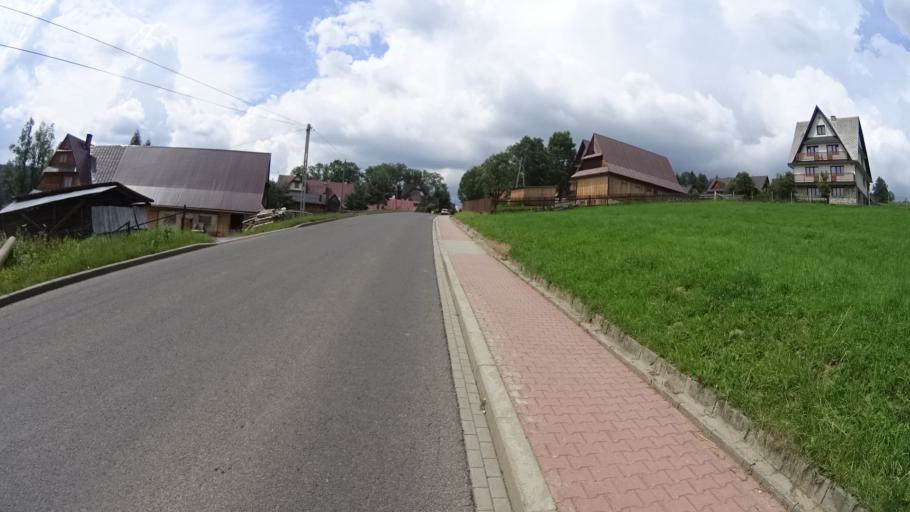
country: PL
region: Lesser Poland Voivodeship
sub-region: Powiat tatrzanski
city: Poronin
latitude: 49.3363
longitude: 19.9757
